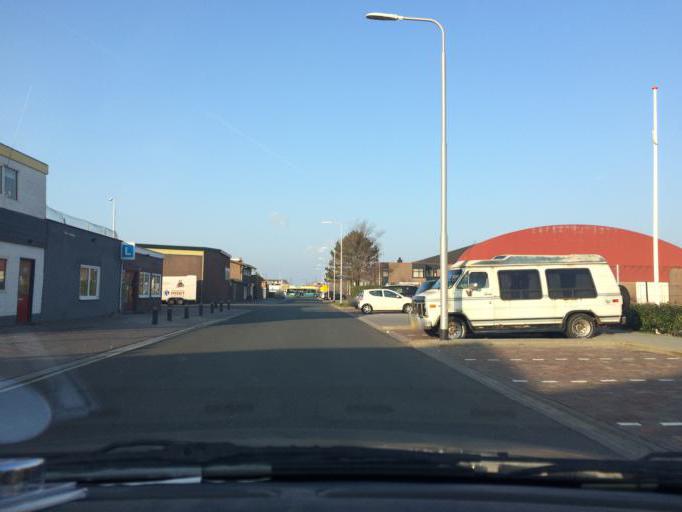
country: NL
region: North Holland
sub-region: Gemeente Bloemendaal
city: Bloemendaal
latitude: 52.4531
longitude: 4.5904
